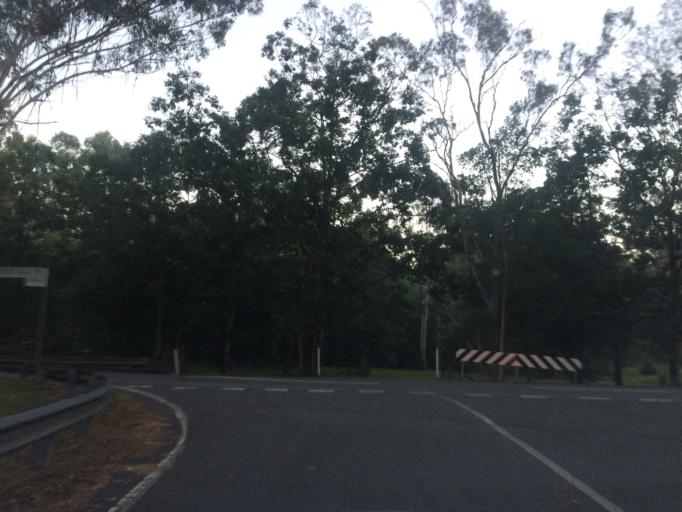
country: AU
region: Queensland
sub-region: Brisbane
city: Kenmore Hills
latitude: -27.4970
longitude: 152.9195
